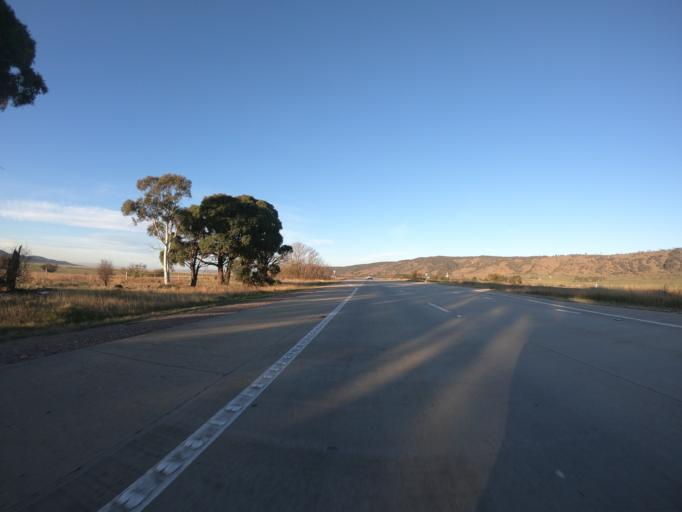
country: AU
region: New South Wales
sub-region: Yass Valley
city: Gundaroo
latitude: -34.9713
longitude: 149.3983
